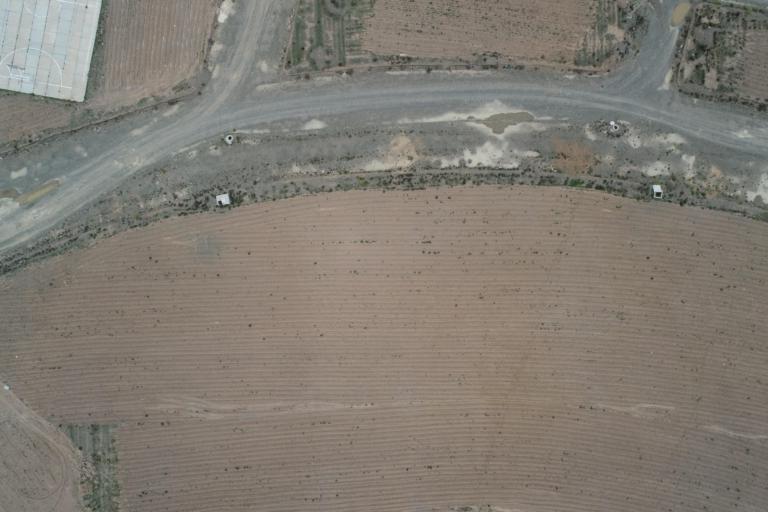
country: BO
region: La Paz
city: La Paz
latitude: -16.5195
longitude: -68.2980
